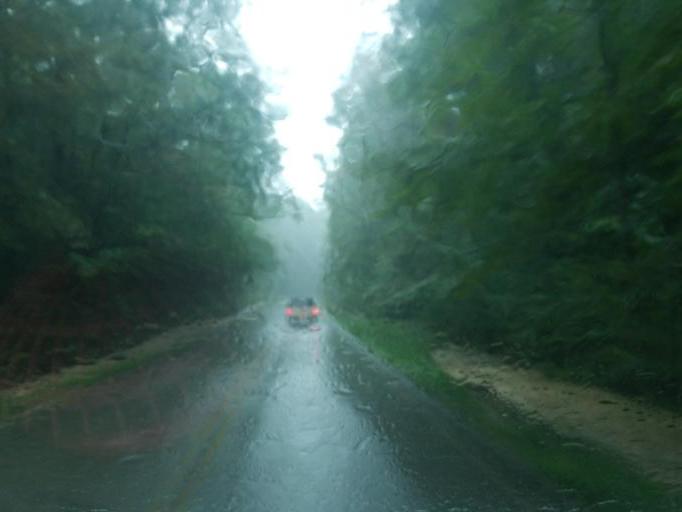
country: US
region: Kentucky
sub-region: Carter County
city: Olive Hill
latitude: 38.3517
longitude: -83.2025
